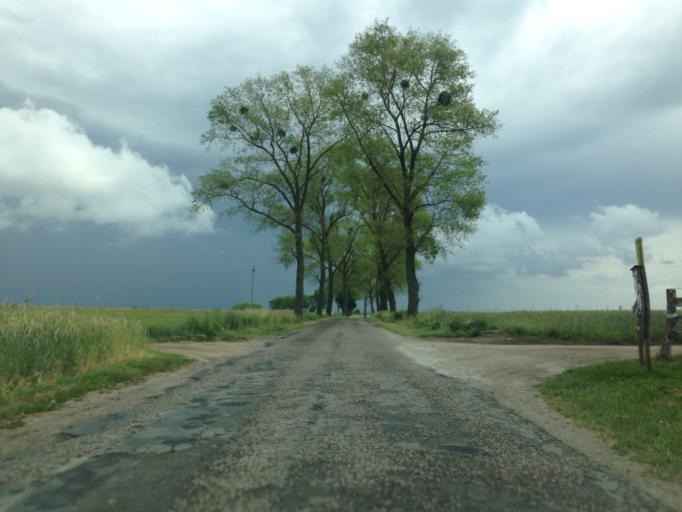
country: PL
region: Kujawsko-Pomorskie
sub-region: Powiat brodnicki
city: Gorzno
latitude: 53.1962
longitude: 19.6188
